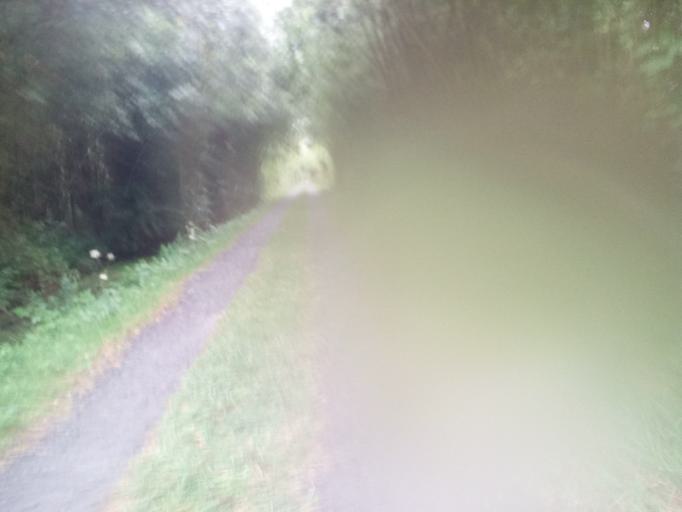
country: FR
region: Lower Normandy
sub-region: Departement du Calvados
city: Bavent
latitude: 49.2335
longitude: -0.1615
